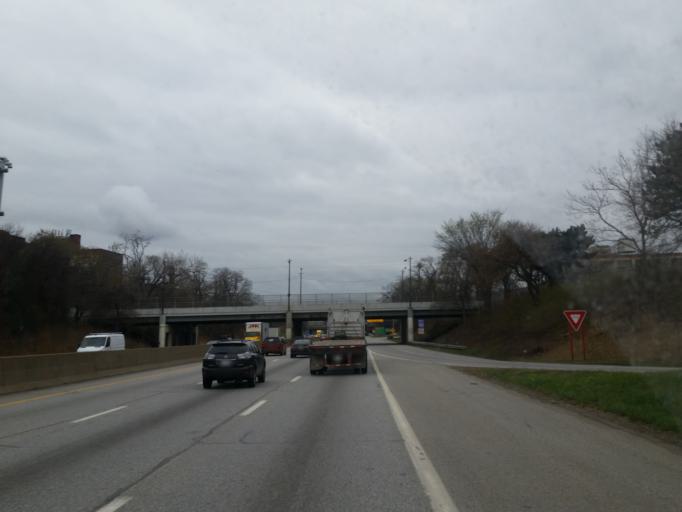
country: US
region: Ohio
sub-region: Cuyahoga County
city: Cleveland
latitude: 41.5084
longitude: -81.6717
